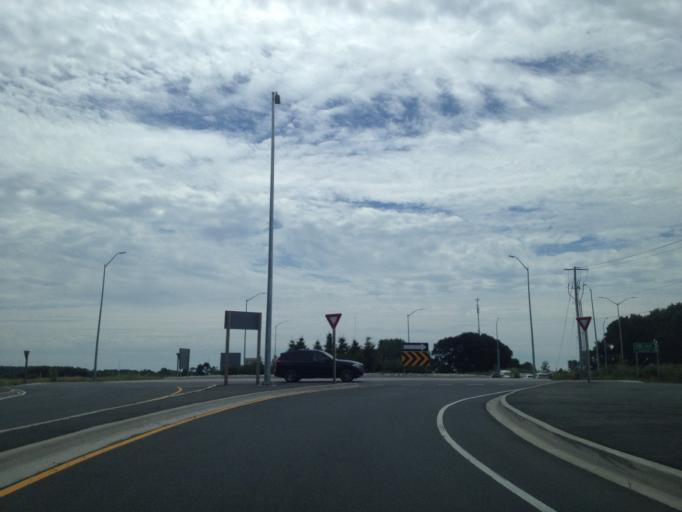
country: CA
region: Ontario
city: Ingersoll
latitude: 43.0289
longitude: -80.8560
